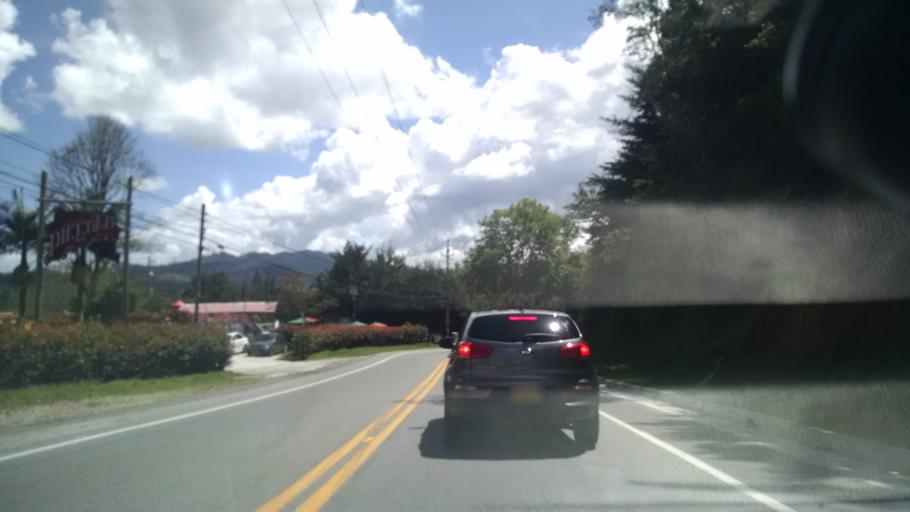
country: CO
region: Antioquia
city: El Retiro
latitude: 6.1217
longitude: -75.5007
